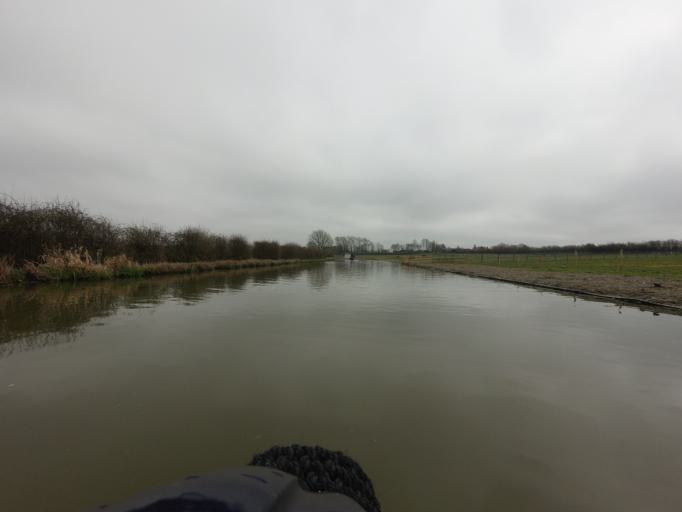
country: GB
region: England
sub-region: Central Bedfordshire
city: Leighton Buzzard
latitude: 51.8963
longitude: -0.6684
